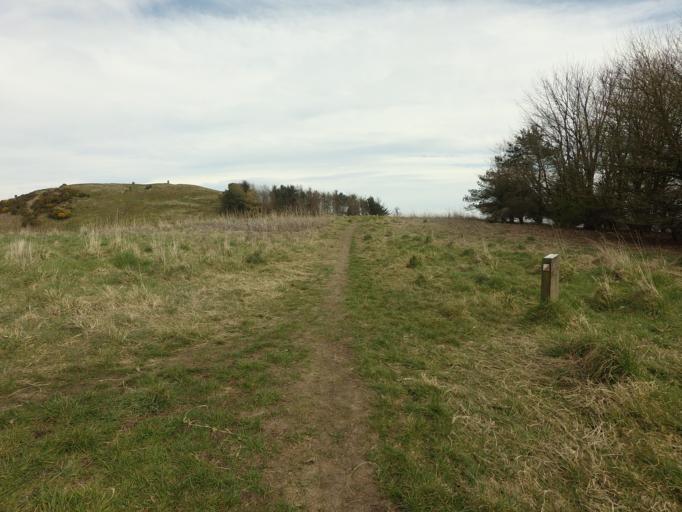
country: GB
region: Scotland
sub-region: West Lothian
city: Livingston
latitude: 55.9106
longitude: -3.5493
